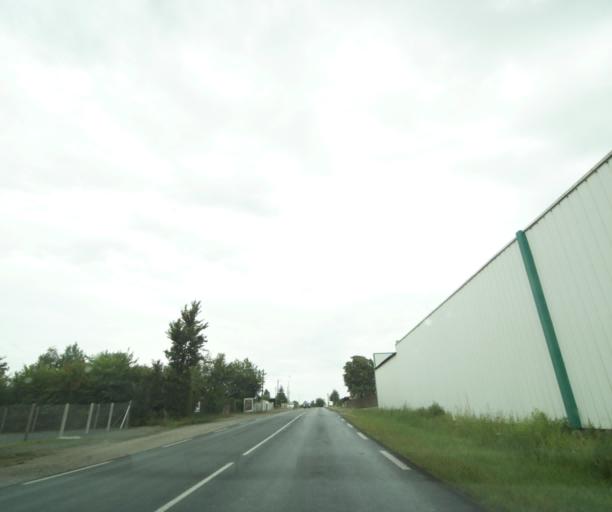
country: FR
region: Poitou-Charentes
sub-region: Departement des Deux-Sevres
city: Chatillon-sur-Thouet
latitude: 46.6714
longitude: -0.2456
